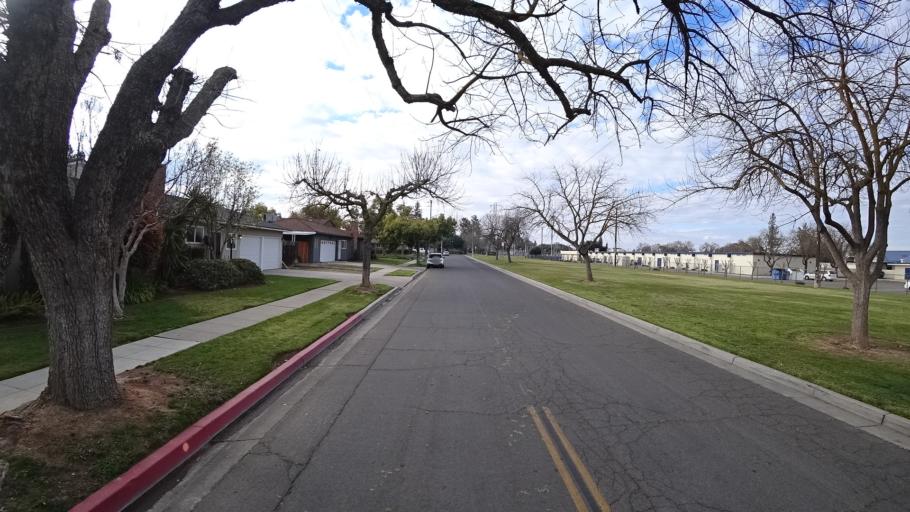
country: US
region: California
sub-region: Fresno County
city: Clovis
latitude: 36.8265
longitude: -119.7677
